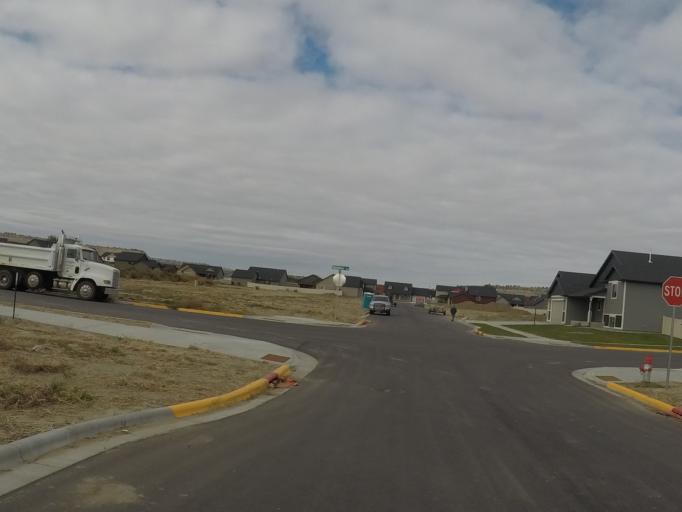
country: US
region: Montana
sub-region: Yellowstone County
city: Laurel
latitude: 45.7782
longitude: -108.6618
